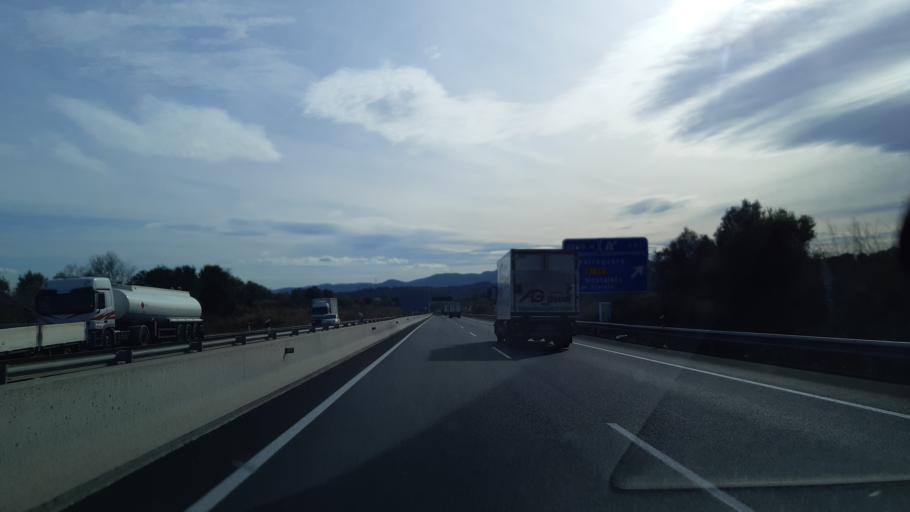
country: ES
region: Catalonia
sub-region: Provincia de Barcelona
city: Esparreguera
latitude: 41.5426
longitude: 1.8558
